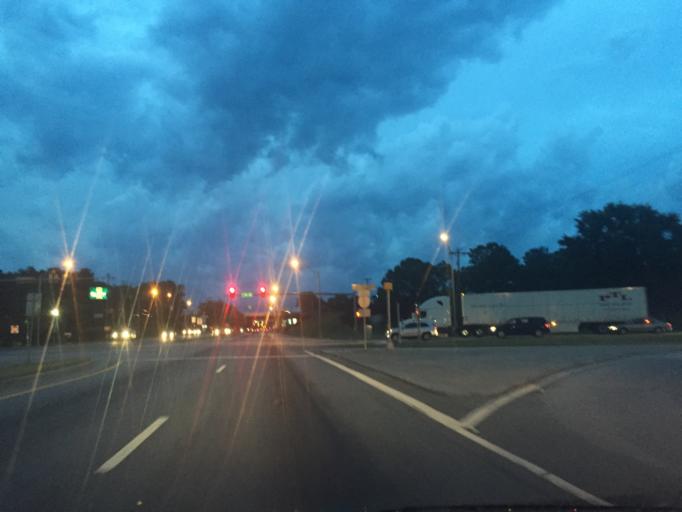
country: US
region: Georgia
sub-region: Bryan County
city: Richmond Hill
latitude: 31.9264
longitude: -81.3330
